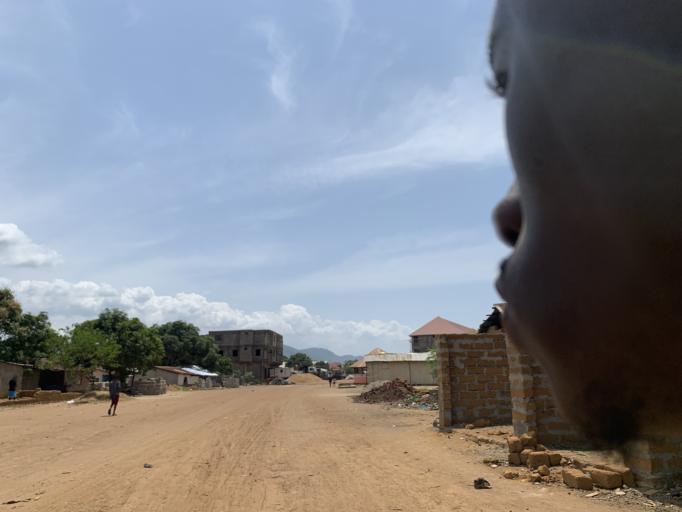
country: SL
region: Western Area
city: Waterloo
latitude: 8.3354
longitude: -13.0406
